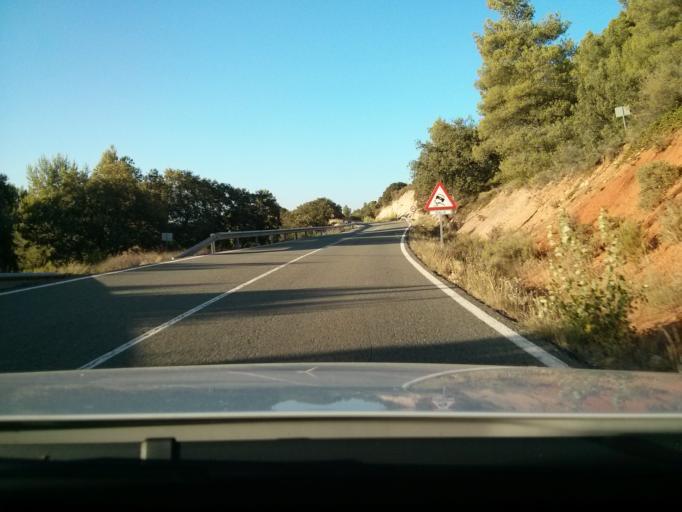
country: ES
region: Castille-La Mancha
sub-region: Provincia de Guadalajara
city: Chillaron del Rey
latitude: 40.6111
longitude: -2.6901
